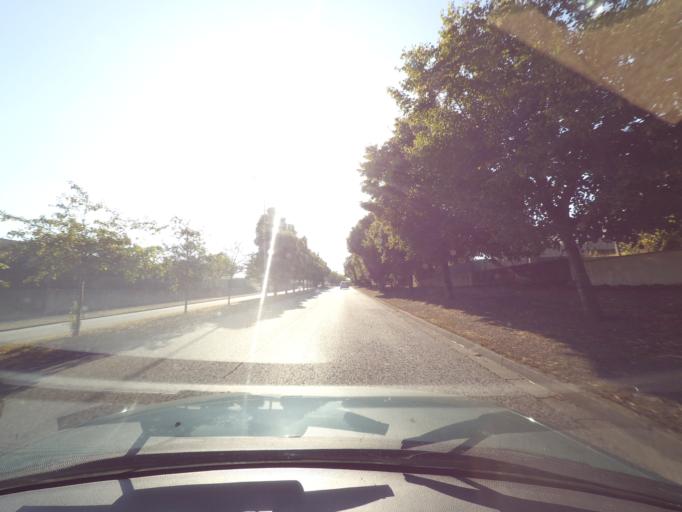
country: FR
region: Poitou-Charentes
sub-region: Departement des Deux-Sevres
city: Chatillon-sur-Thouet
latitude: 46.6537
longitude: -0.2337
